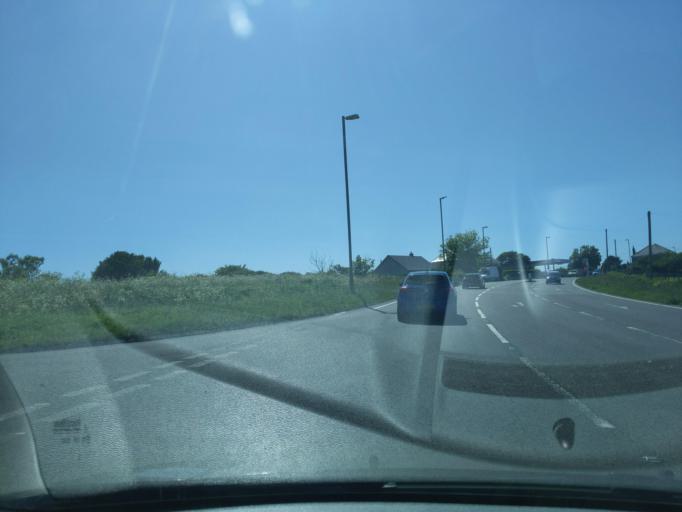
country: GB
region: England
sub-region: Cornwall
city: Penryn
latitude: 50.1641
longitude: -5.1561
